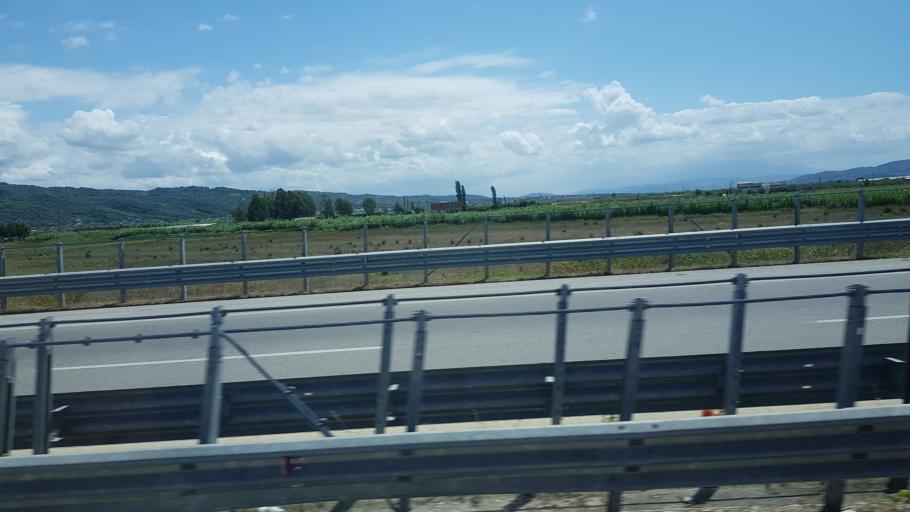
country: AL
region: Fier
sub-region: Rrethi i Fierit
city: Levan
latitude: 40.6637
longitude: 19.4752
